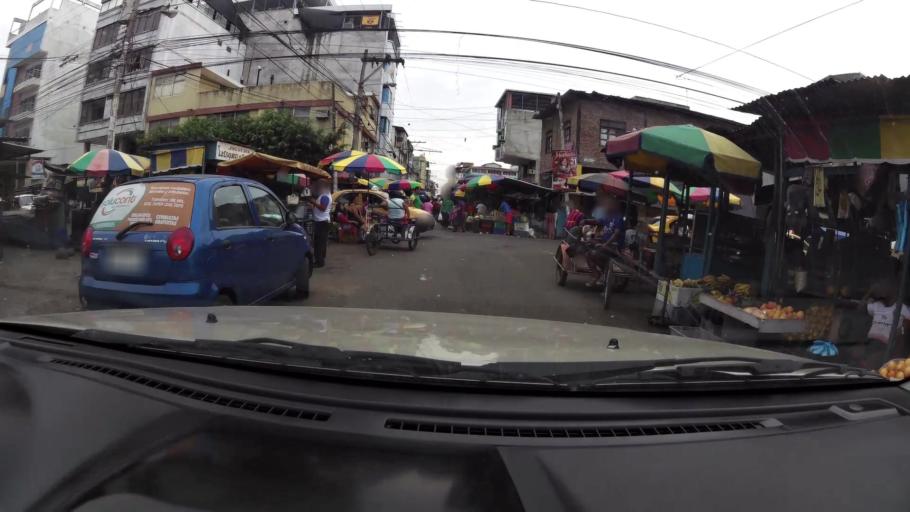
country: EC
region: El Oro
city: Machala
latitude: -3.2574
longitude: -79.9562
